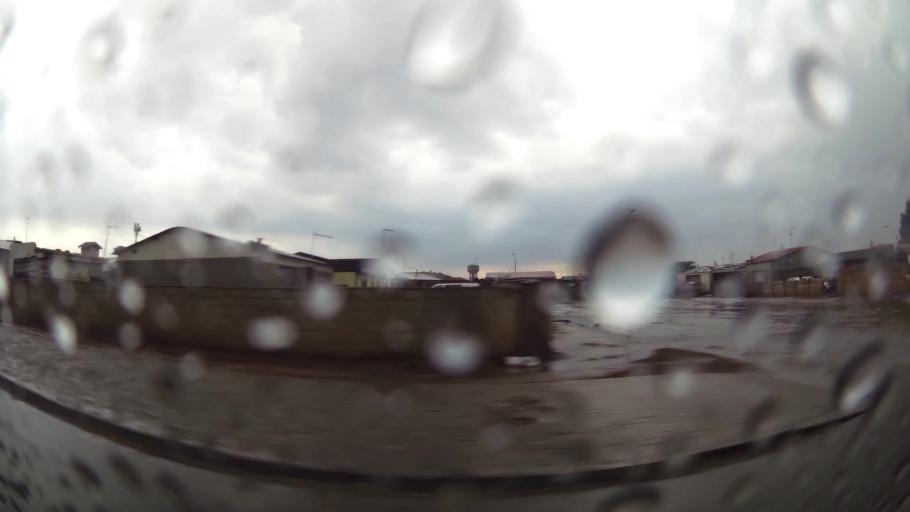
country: ZA
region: Gauteng
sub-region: Ekurhuleni Metropolitan Municipality
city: Germiston
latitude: -26.3455
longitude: 28.1364
